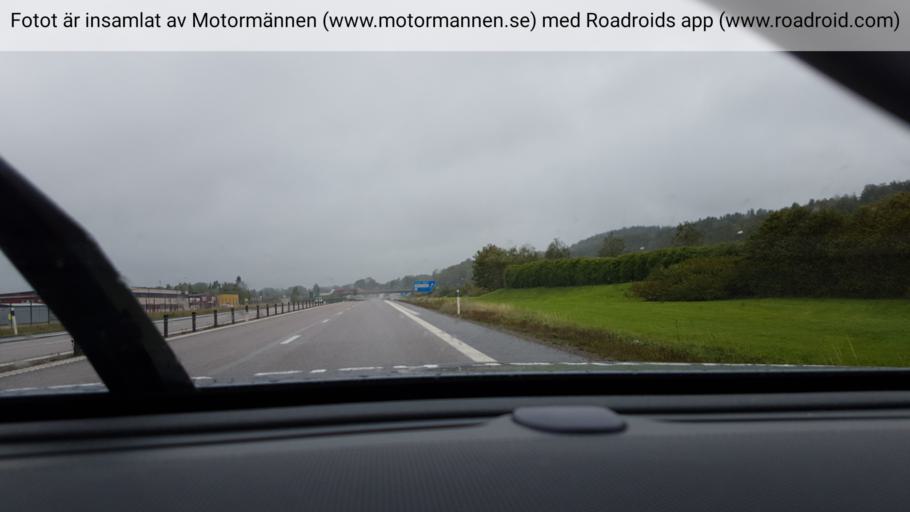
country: SE
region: Vaestra Goetaland
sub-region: Lilla Edets Kommun
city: Lilla Edet
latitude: 58.1201
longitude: 12.1396
